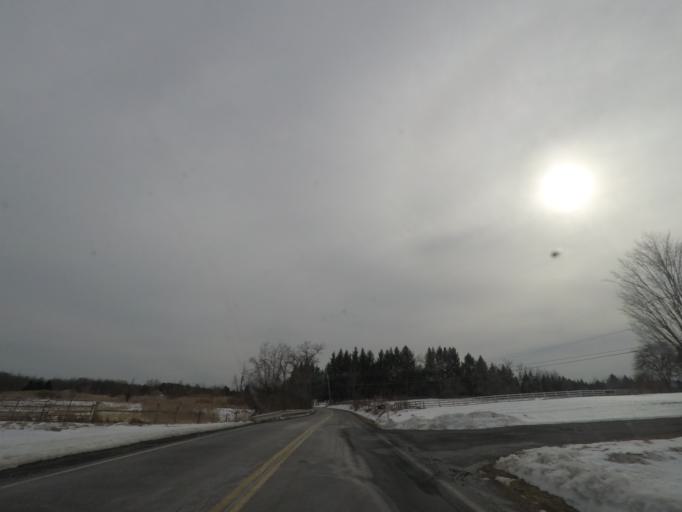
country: US
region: New York
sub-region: Albany County
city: Altamont
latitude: 42.6886
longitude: -73.9843
